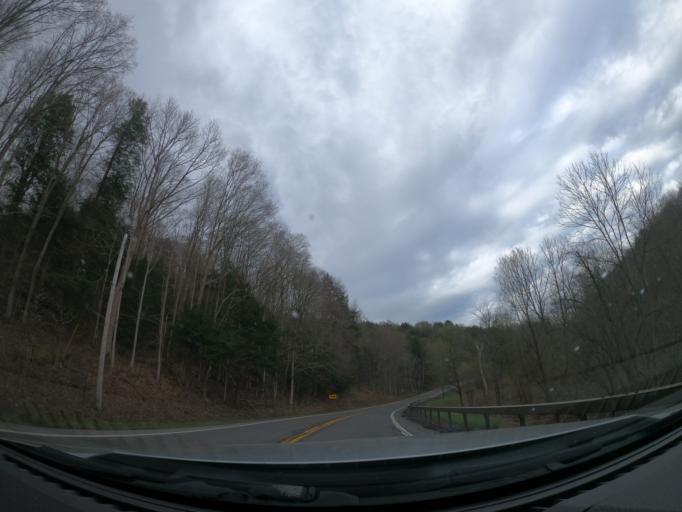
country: US
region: New York
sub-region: Madison County
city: Cazenovia
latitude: 42.7992
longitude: -75.8415
